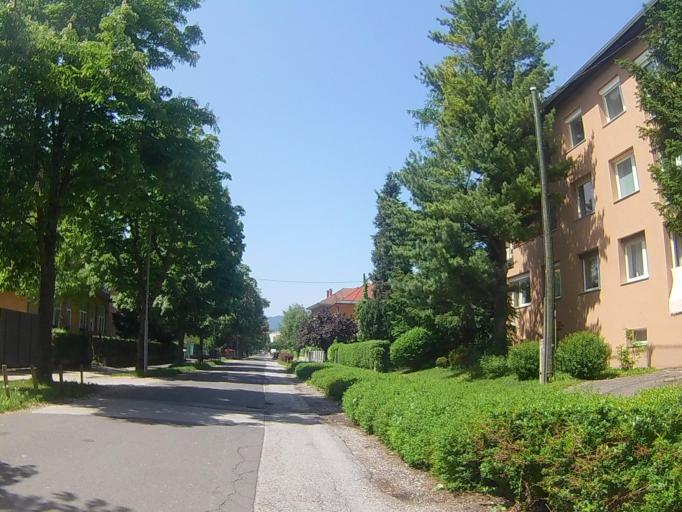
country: SI
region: Maribor
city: Maribor
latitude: 46.5642
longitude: 15.6435
